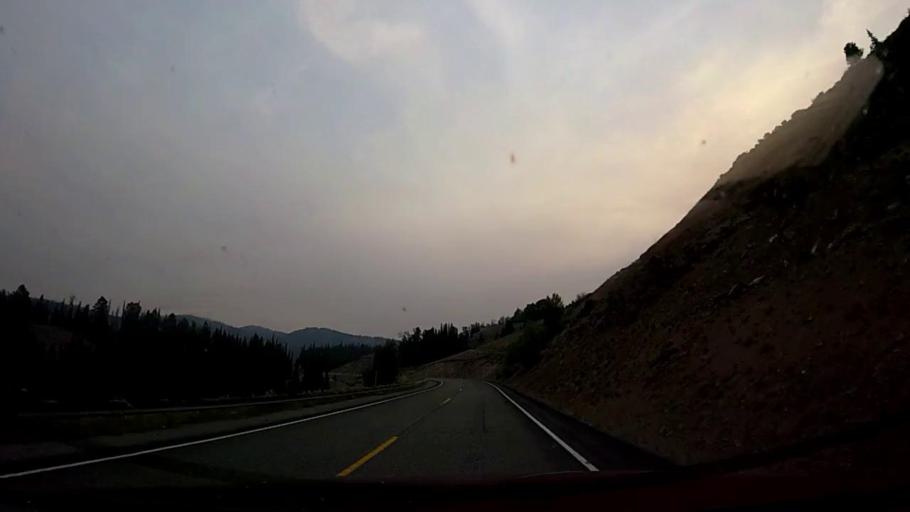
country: US
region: Idaho
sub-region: Blaine County
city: Ketchum
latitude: 43.8777
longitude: -114.7032
